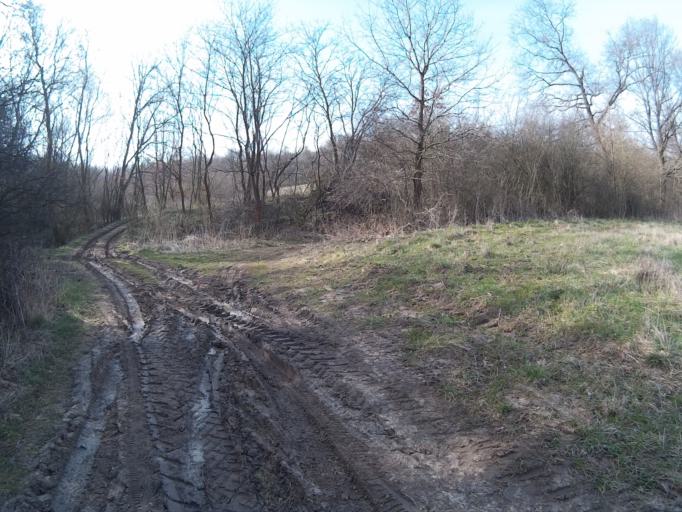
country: HU
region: Nograd
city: Retsag
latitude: 47.8831
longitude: 19.1881
